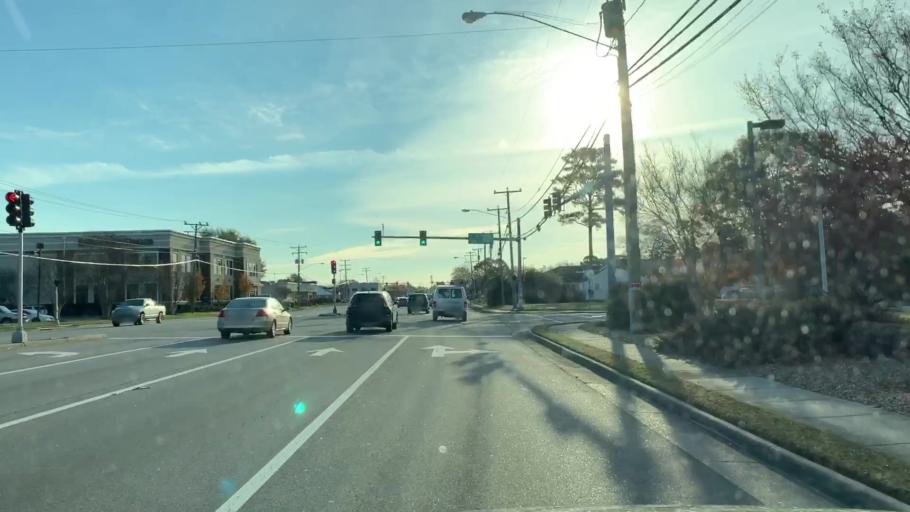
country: US
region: Virginia
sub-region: City of Chesapeake
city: Chesapeake
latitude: 36.8010
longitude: -76.1822
